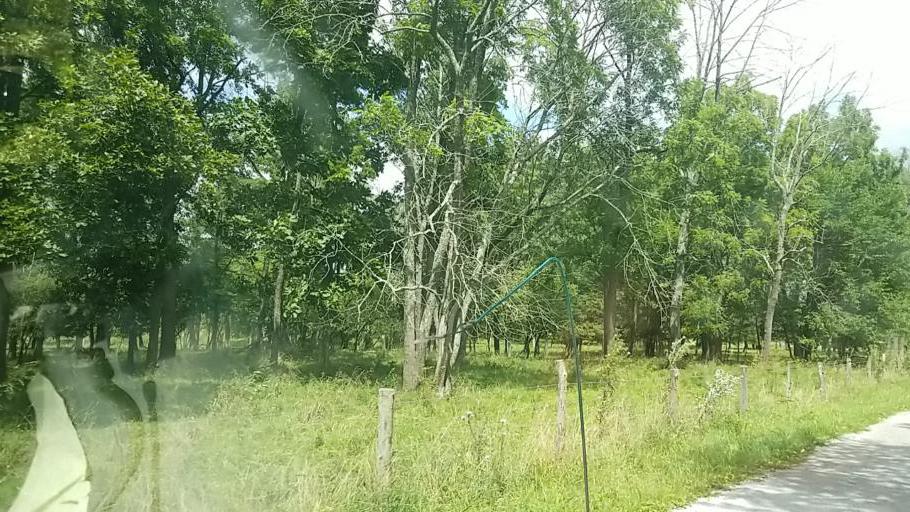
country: US
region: Ohio
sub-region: Clark County
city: South Charleston
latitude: 39.8176
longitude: -83.7218
